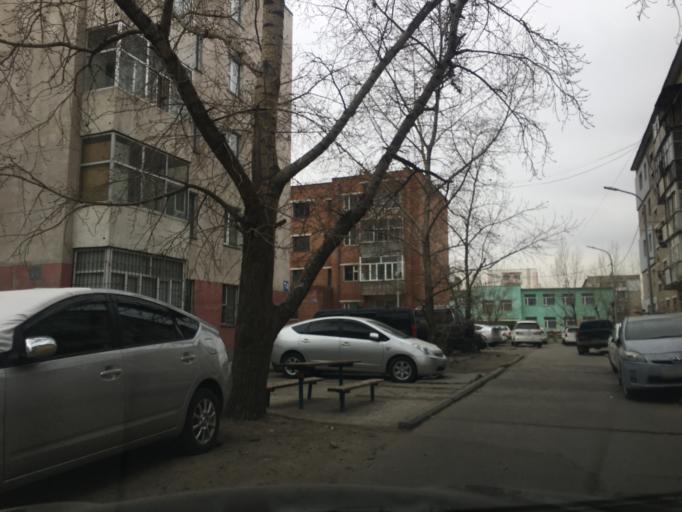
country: MN
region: Ulaanbaatar
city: Ulaanbaatar
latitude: 47.9104
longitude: 106.8881
